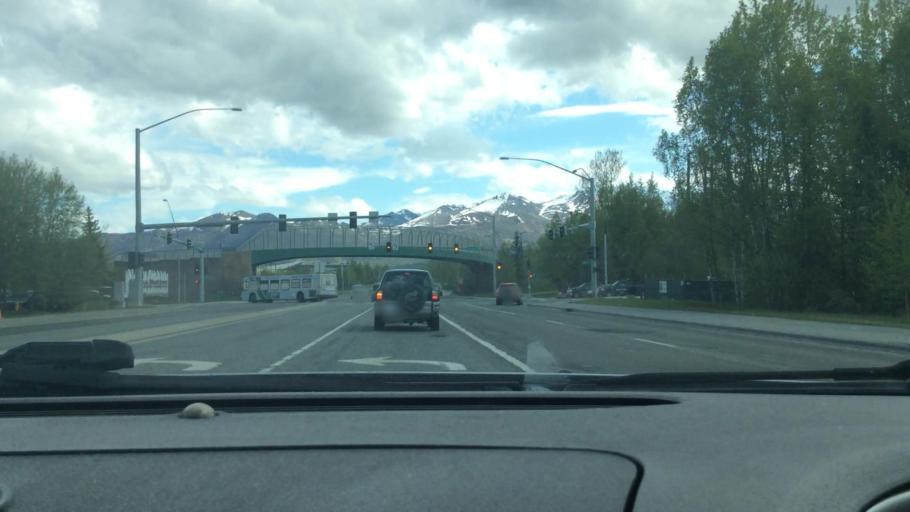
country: US
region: Alaska
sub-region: Anchorage Municipality
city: Anchorage
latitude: 61.1808
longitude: -149.8100
